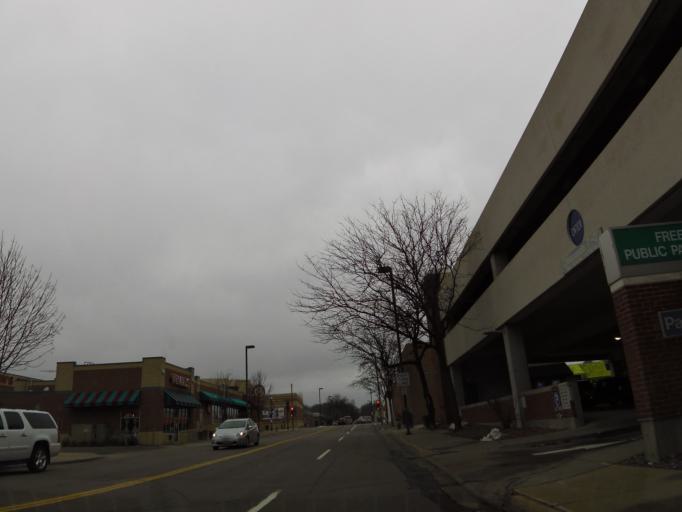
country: US
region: Minnesota
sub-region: Hennepin County
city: Minnetonka Mills
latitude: 44.9235
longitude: -93.4140
